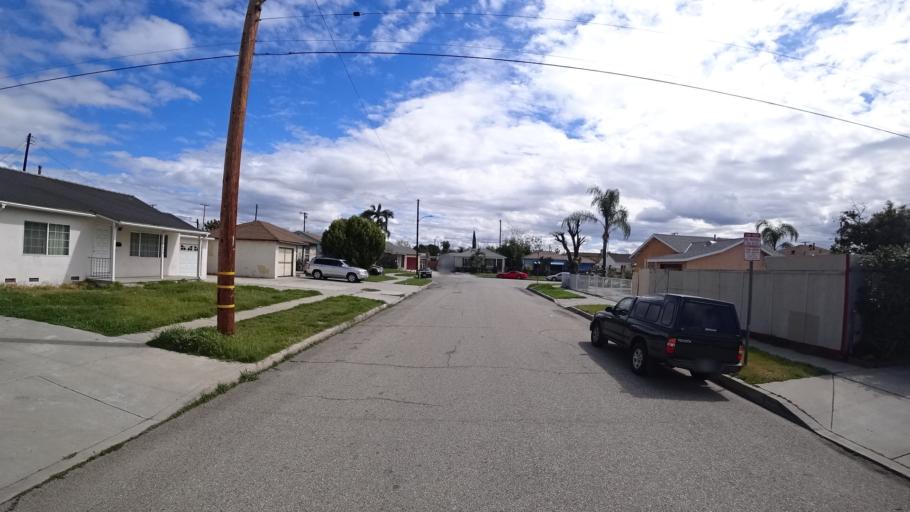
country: US
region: California
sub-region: Los Angeles County
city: Baldwin Park
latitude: 34.0986
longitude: -117.9680
